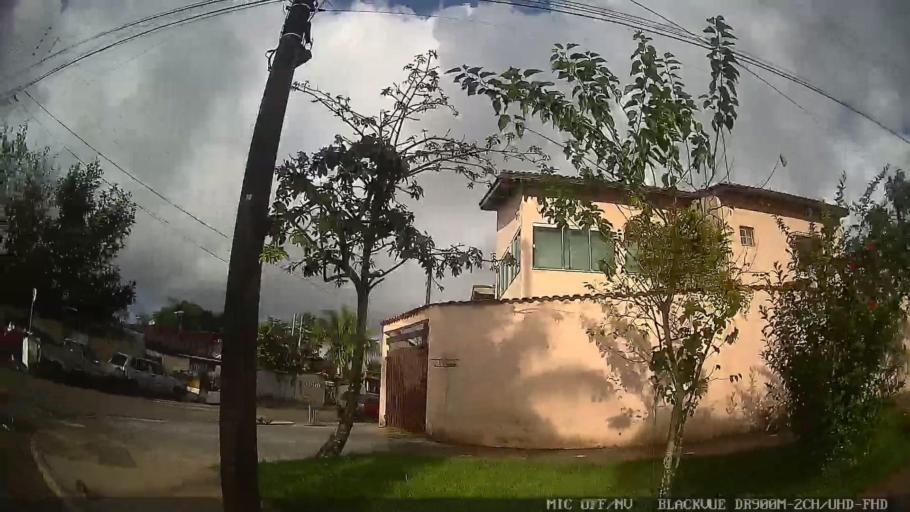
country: BR
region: Sao Paulo
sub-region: Itanhaem
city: Itanhaem
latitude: -24.2029
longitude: -46.8725
